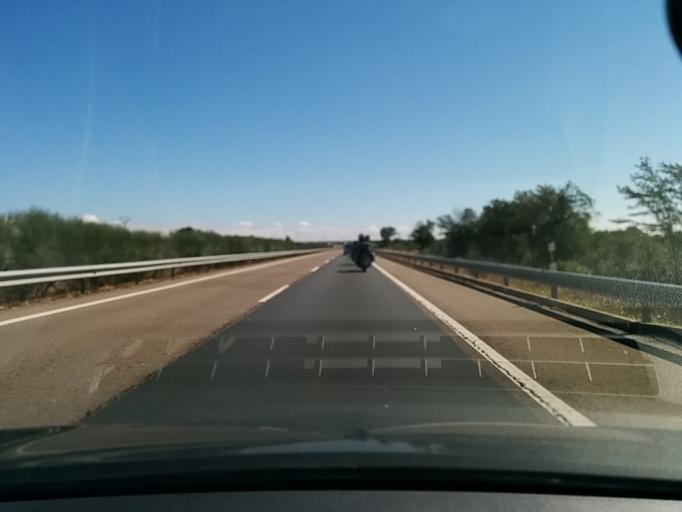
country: ES
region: Aragon
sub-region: Provincia de Huesca
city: Almudebar
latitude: 42.0279
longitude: -0.5955
